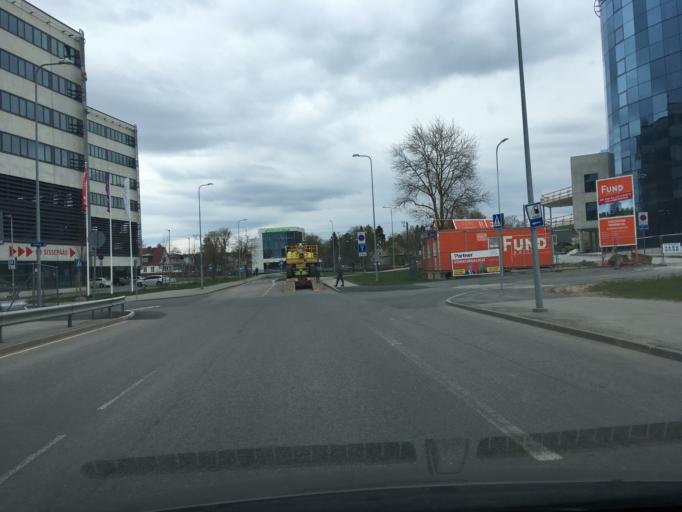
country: EE
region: Harju
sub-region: Tallinna linn
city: Tallinn
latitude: 59.4180
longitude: 24.7522
